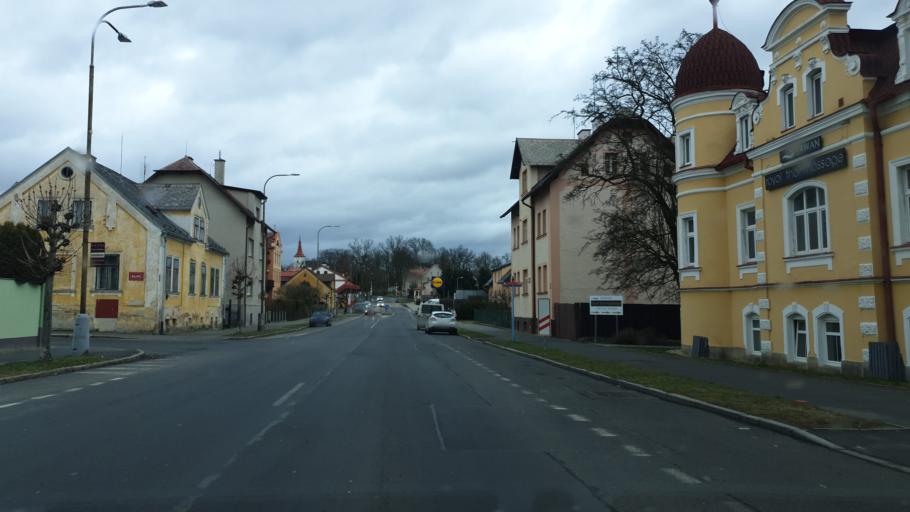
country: CZ
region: Karlovarsky
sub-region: Okres Cheb
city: Frantiskovy Lazne
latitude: 50.1260
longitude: 12.3466
